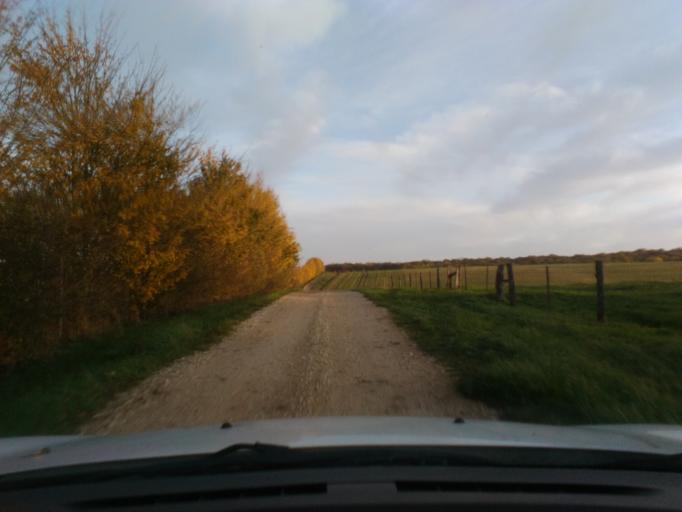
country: FR
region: Lorraine
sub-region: Departement des Vosges
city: Mirecourt
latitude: 48.2543
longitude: 6.1723
